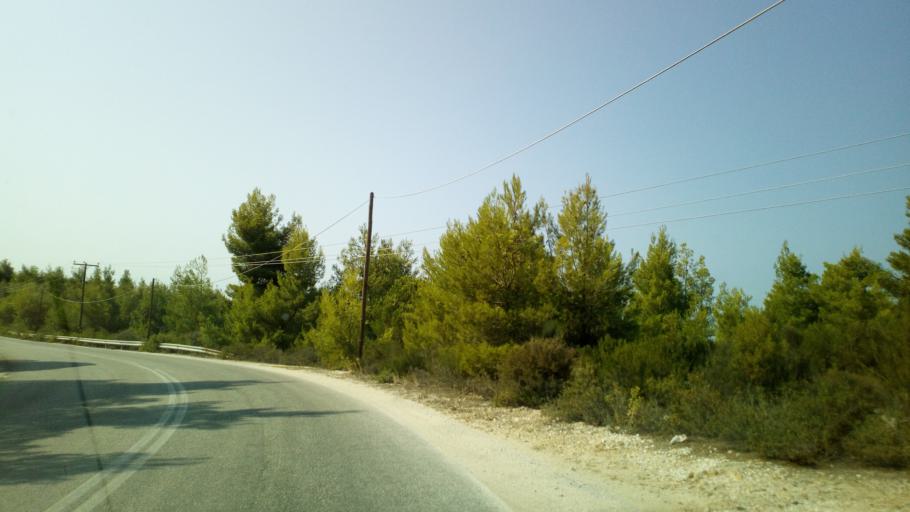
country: GR
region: Central Macedonia
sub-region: Nomos Chalkidikis
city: Sarti
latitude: 40.1161
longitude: 23.9783
